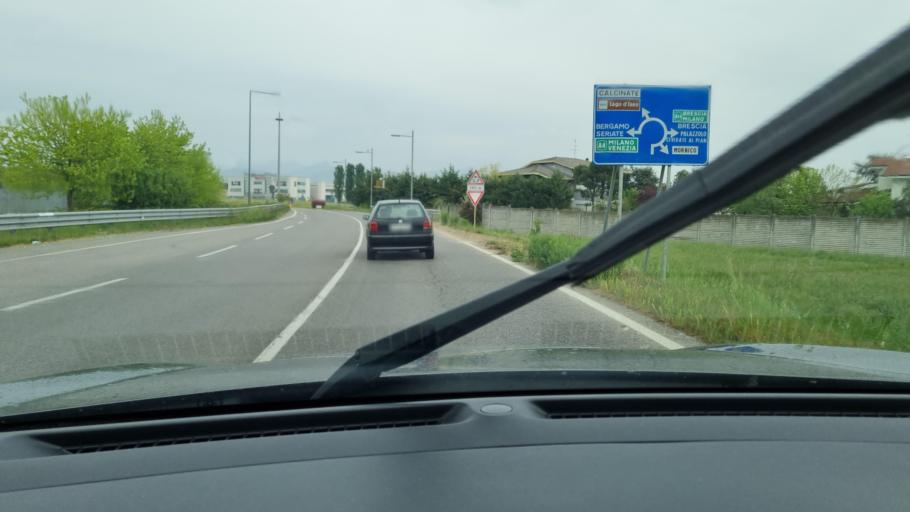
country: IT
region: Lombardy
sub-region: Provincia di Bergamo
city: Mornico al Serio
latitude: 45.6010
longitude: 9.8064
